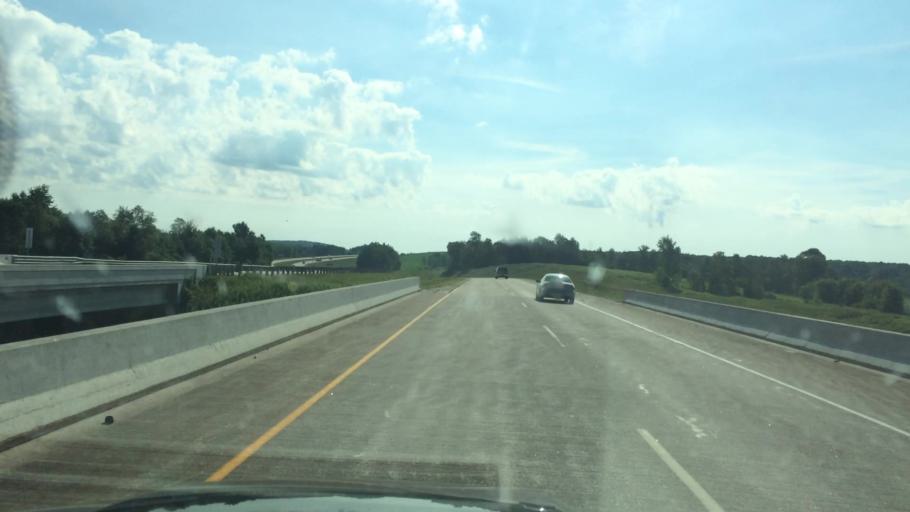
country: US
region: Wisconsin
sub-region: Shawano County
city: Wittenberg
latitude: 44.8235
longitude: -89.1234
